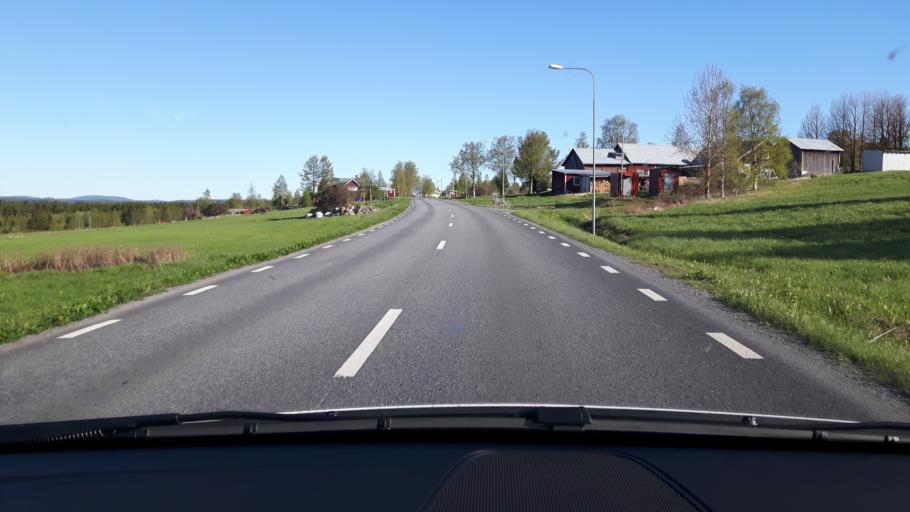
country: SE
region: Jaemtland
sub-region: Stroemsunds Kommun
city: Stroemsund
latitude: 63.8208
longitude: 15.5155
